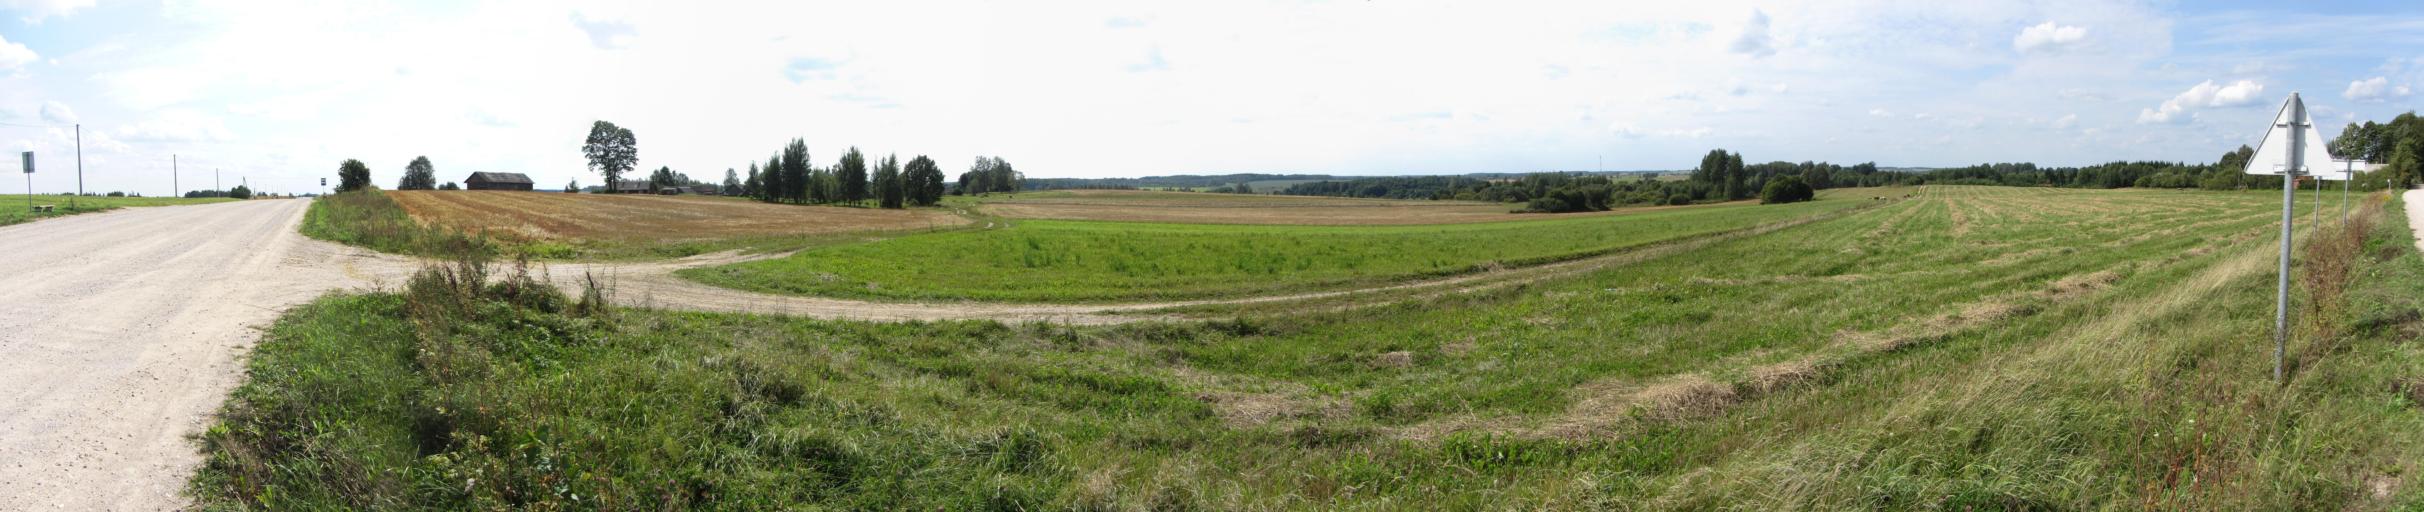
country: LT
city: Salcininkai
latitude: 54.4409
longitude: 25.5395
